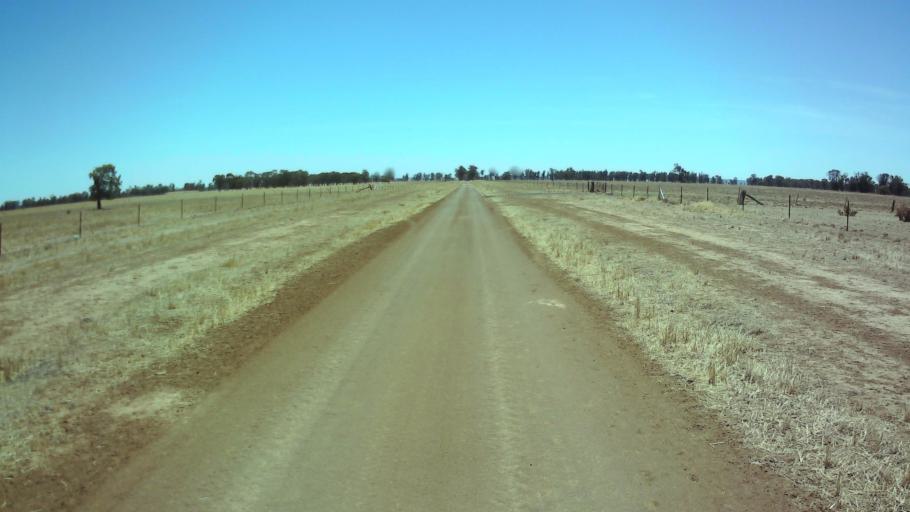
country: AU
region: New South Wales
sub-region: Weddin
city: Grenfell
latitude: -33.9816
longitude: 147.7360
